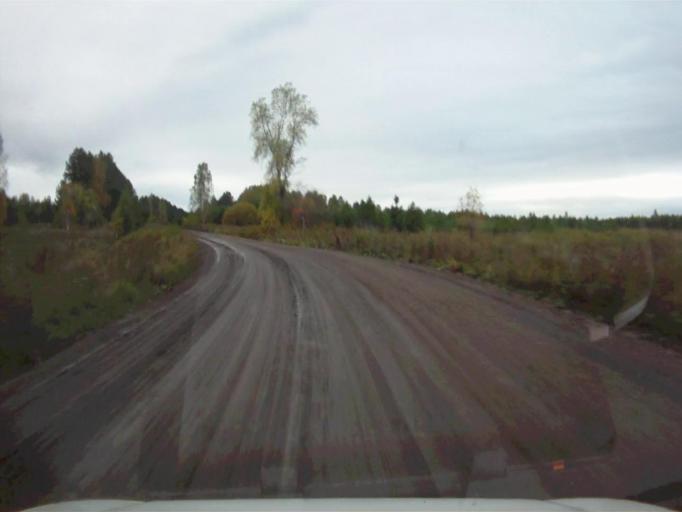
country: RU
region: Chelyabinsk
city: Nyazepetrovsk
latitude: 56.1392
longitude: 59.2979
